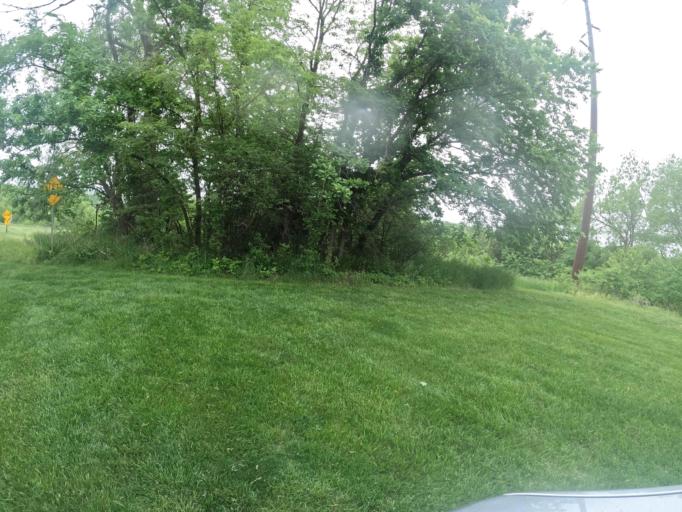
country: US
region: Nebraska
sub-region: Sarpy County
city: Offutt Air Force Base
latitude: 41.0505
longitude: -95.9652
